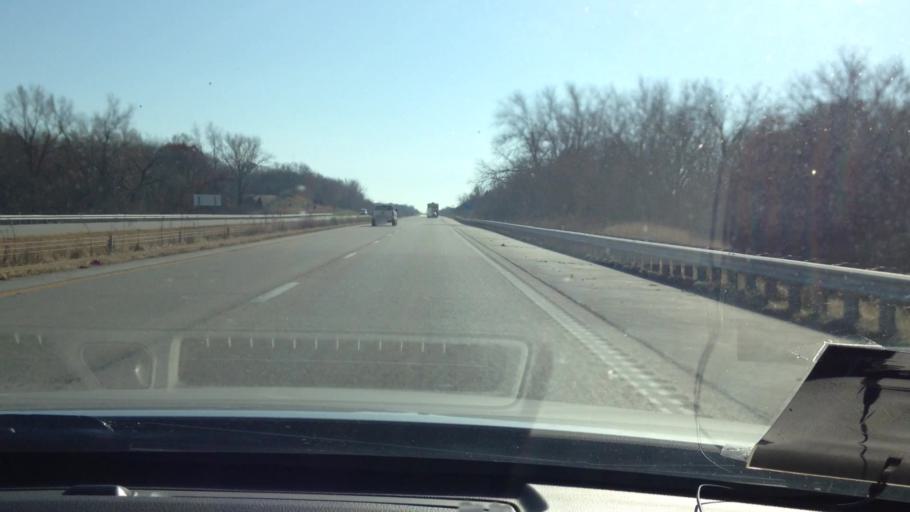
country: US
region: Missouri
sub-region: Platte County
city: Platte City
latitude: 39.4605
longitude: -94.7883
